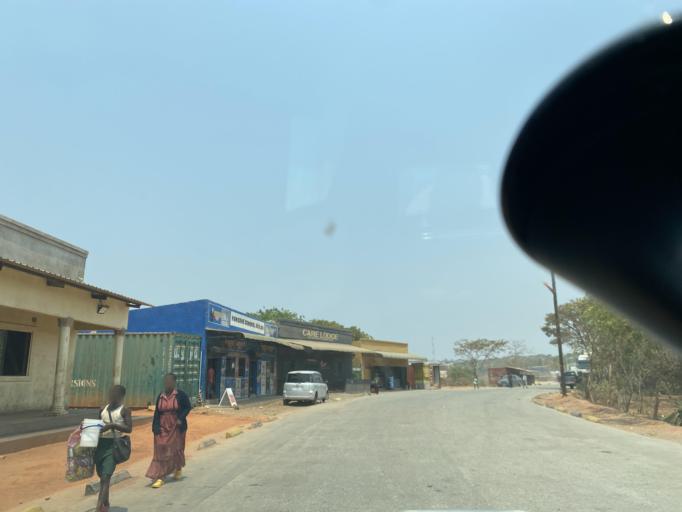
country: ZM
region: Lusaka
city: Lusaka
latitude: -15.5512
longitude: 28.4830
